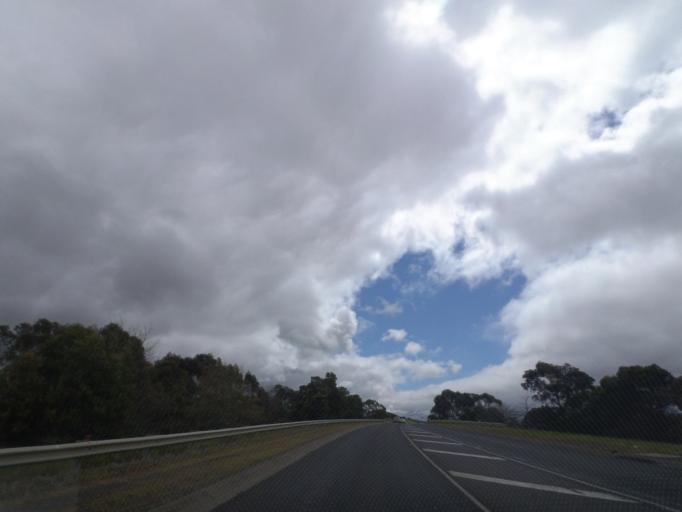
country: AU
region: Victoria
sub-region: Ballarat North
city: Lake Wendouree
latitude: -37.5219
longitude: 143.8443
